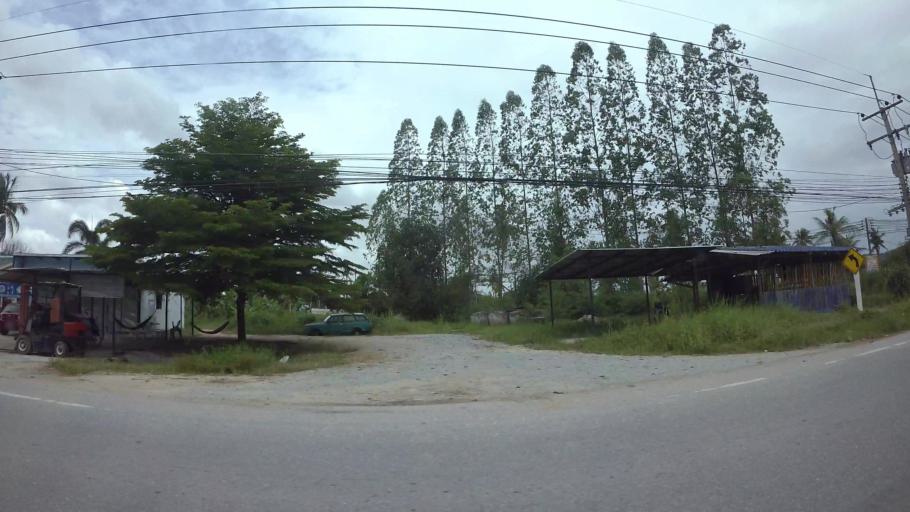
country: TH
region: Chon Buri
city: Si Racha
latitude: 13.1862
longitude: 100.9822
